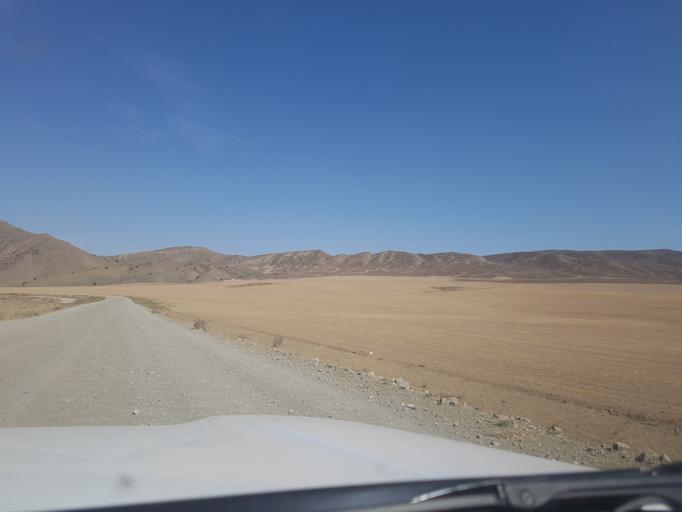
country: TM
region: Ahal
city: Baharly
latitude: 38.4345
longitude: 57.0368
